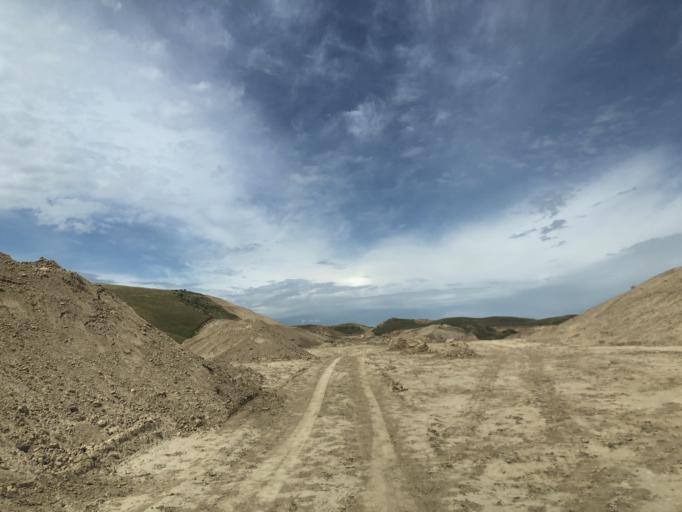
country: KZ
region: Almaty Oblysy
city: Burunday
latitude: 43.2962
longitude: 76.2100
